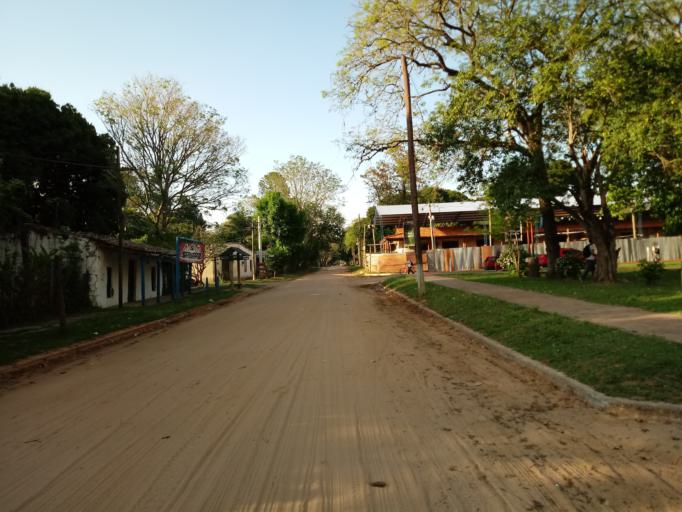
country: AR
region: Corrientes
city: San Luis del Palmar
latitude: -27.4552
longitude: -58.6553
